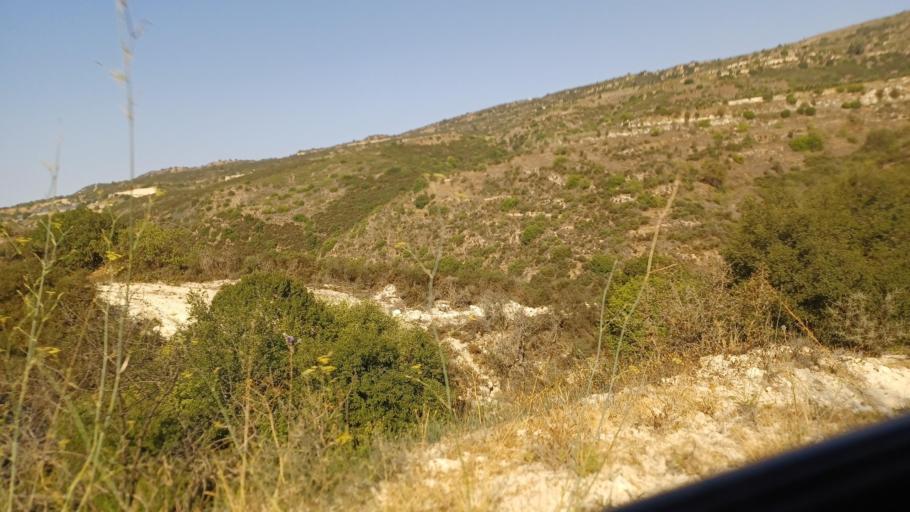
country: CY
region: Pafos
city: Tala
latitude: 34.8863
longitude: 32.4538
